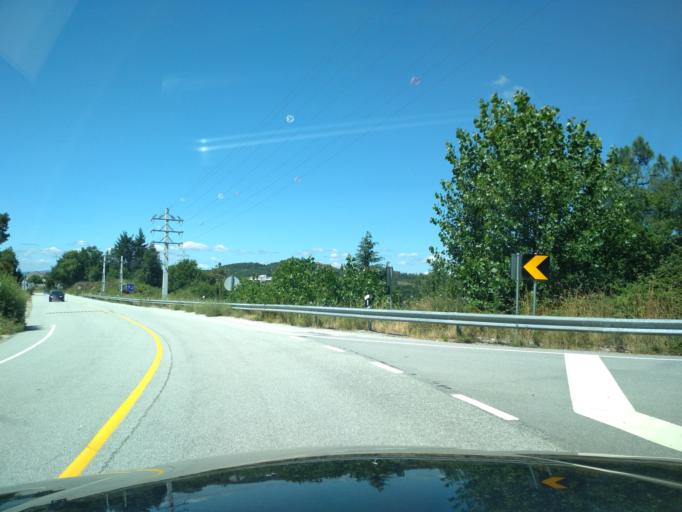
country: PT
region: Vila Real
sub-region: Ribeira de Pena
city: Ribeira de Pena
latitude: 41.5034
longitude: -7.7850
